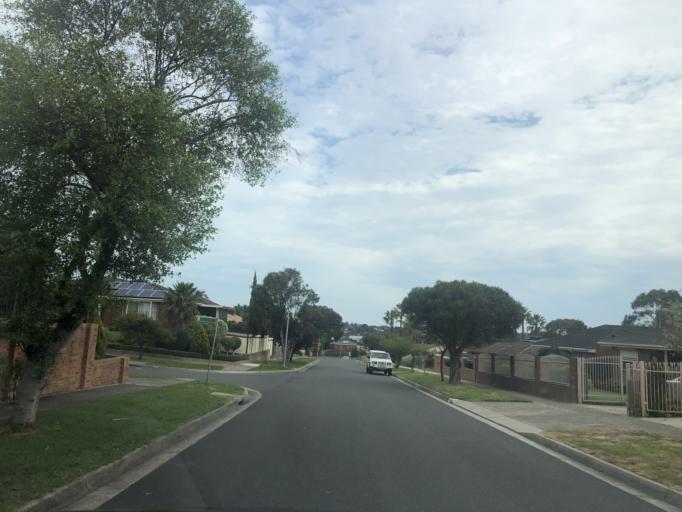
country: AU
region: Victoria
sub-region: Casey
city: Hallam
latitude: -38.0141
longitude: 145.2761
